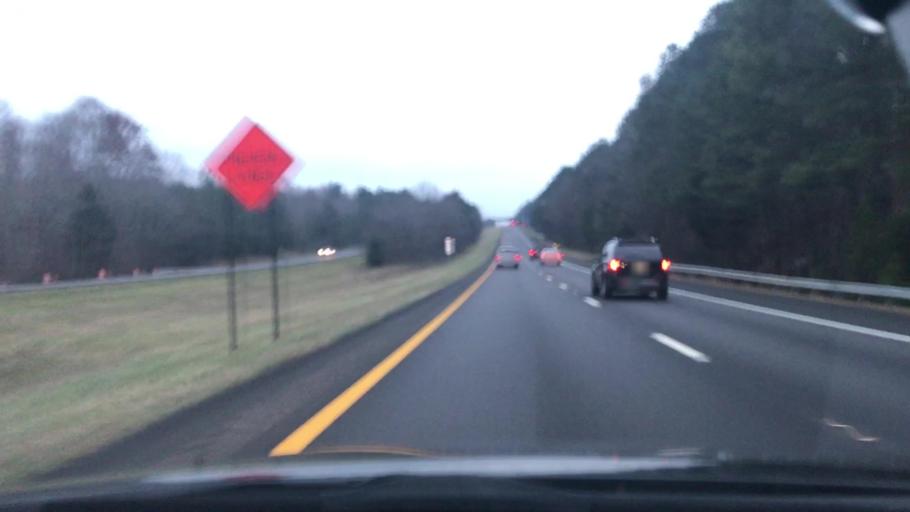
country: US
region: Tennessee
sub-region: Sumner County
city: White House
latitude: 36.4430
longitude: -86.7019
